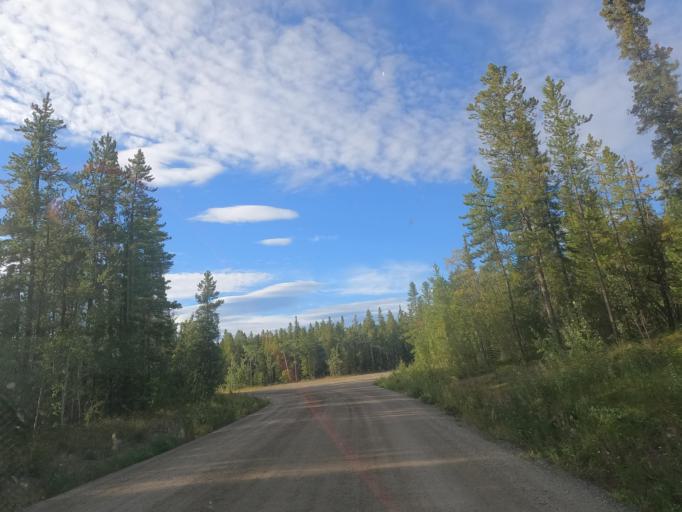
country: CA
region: Yukon
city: Whitehorse
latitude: 60.7577
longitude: -135.0373
